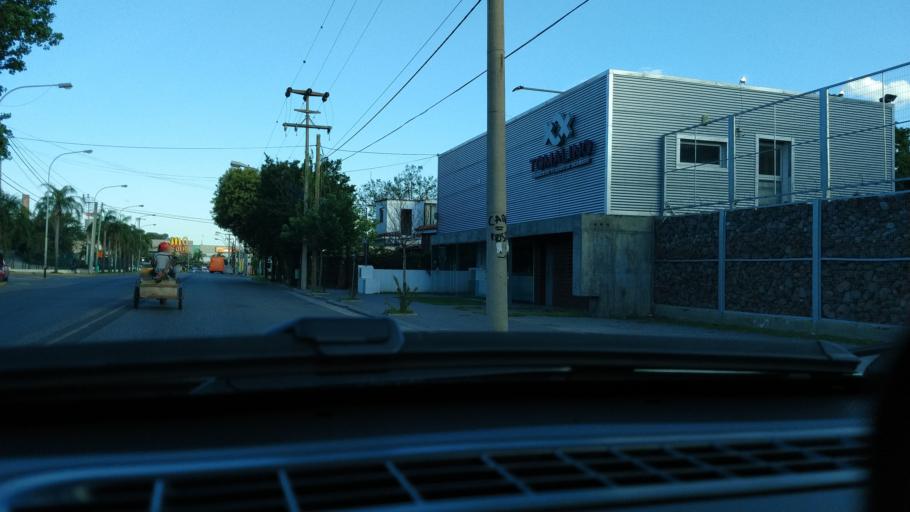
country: AR
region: Cordoba
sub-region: Departamento de Capital
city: Cordoba
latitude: -31.3652
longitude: -64.2227
